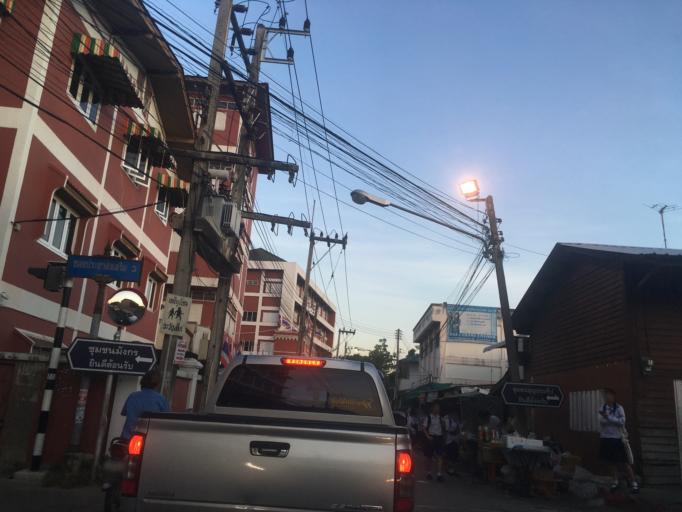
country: TH
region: Chon Buri
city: Ban Bueng
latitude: 13.3111
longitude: 101.1176
